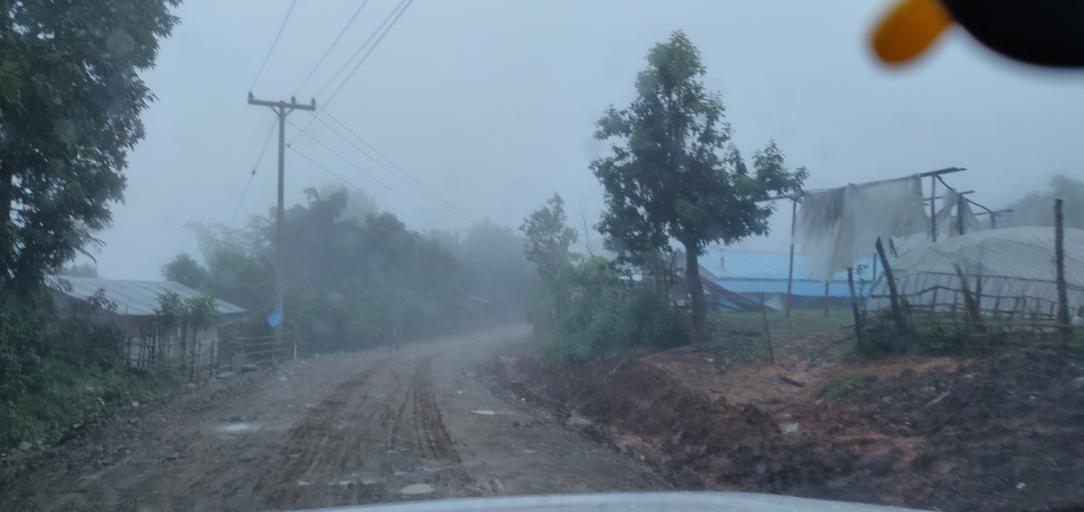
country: LA
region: Phongsali
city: Phongsali
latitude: 21.4225
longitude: 102.2532
